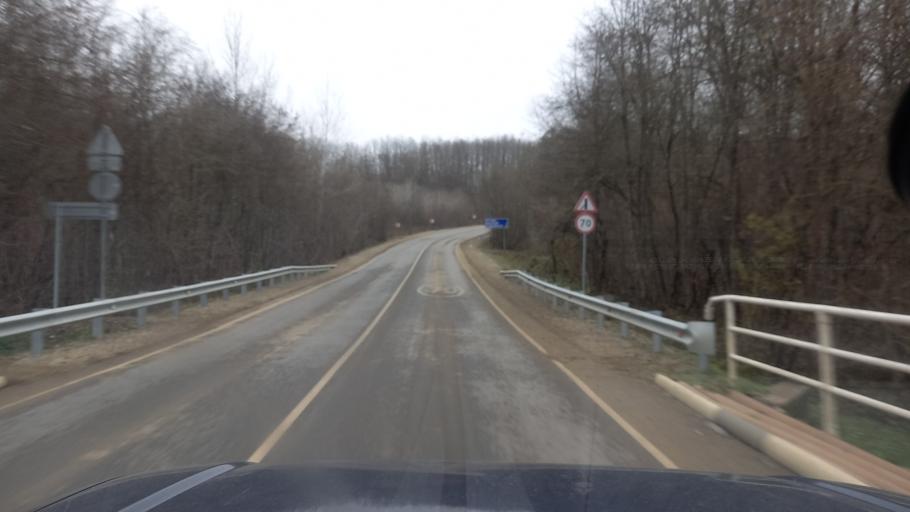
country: RU
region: Krasnodarskiy
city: Saratovskaya
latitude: 44.5432
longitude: 39.2962
